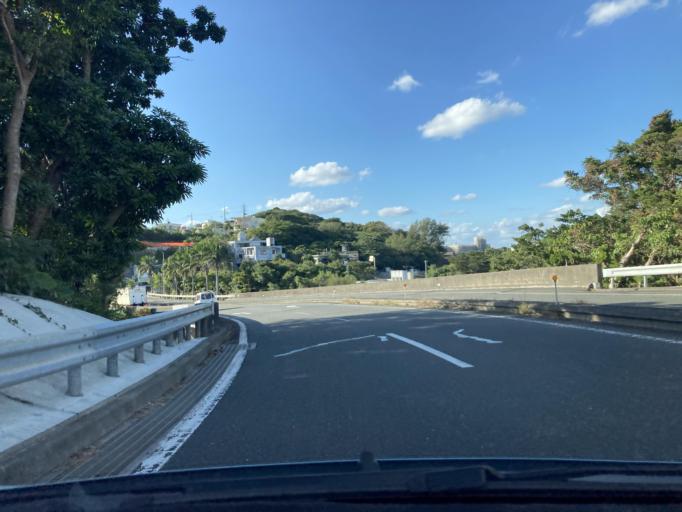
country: JP
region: Okinawa
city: Chatan
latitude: 26.2918
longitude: 127.7862
